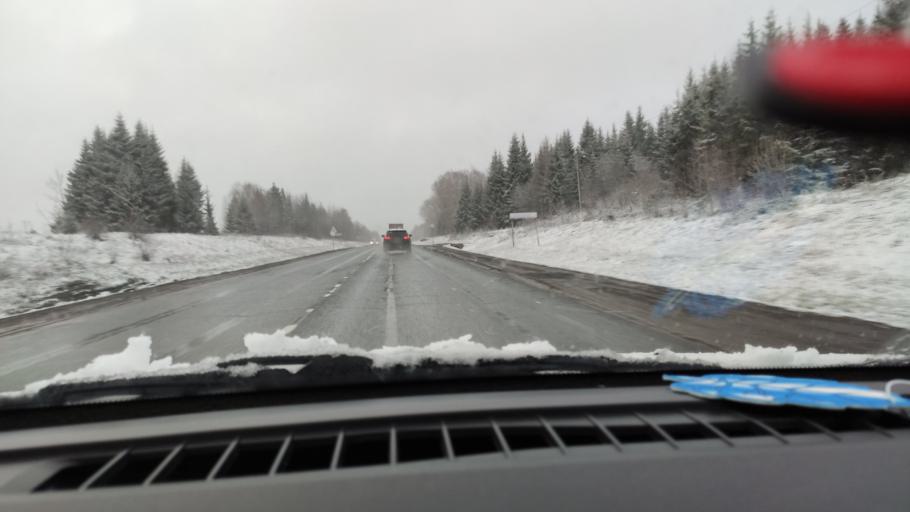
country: RU
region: Perm
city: Kukushtan
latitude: 57.6217
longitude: 56.4807
